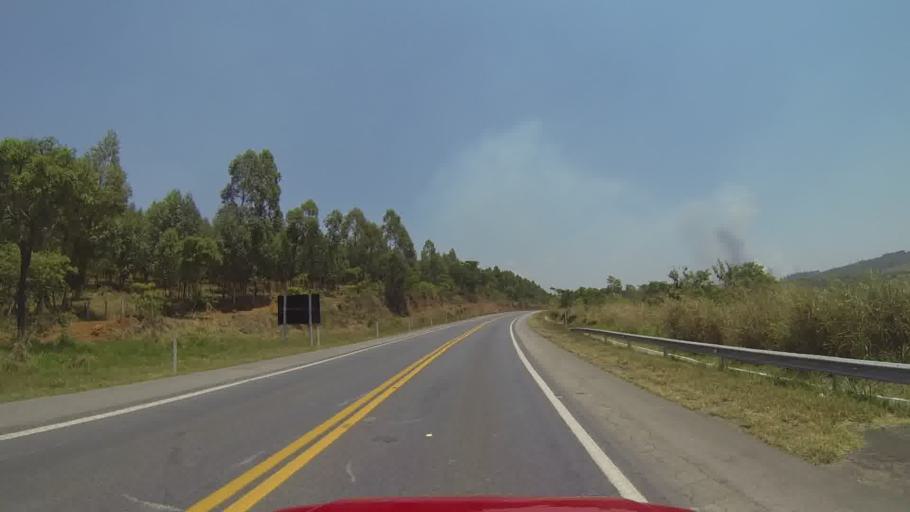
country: BR
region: Minas Gerais
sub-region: Itapecerica
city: Itapecerica
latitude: -20.3430
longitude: -45.2536
